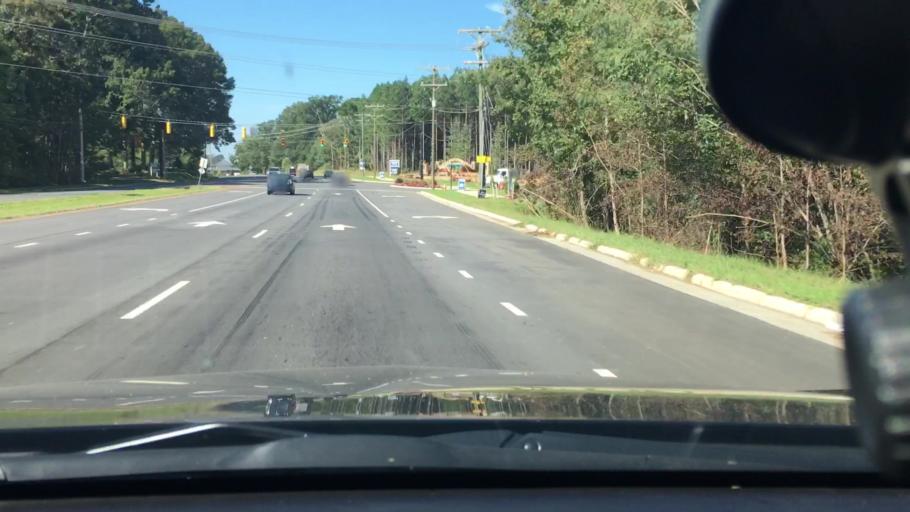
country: US
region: North Carolina
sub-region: Mecklenburg County
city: Mint Hill
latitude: 35.2233
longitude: -80.6400
